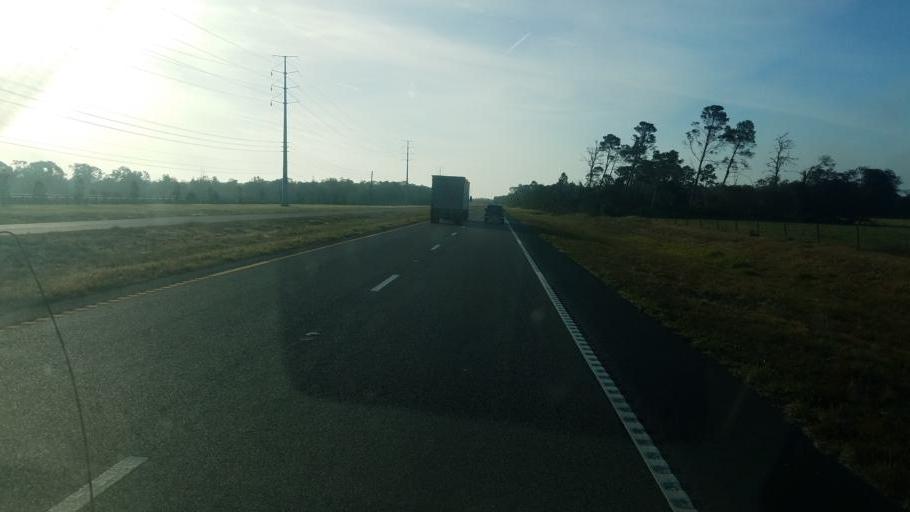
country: US
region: Florida
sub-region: Osceola County
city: Saint Cloud
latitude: 28.2096
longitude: -81.1728
